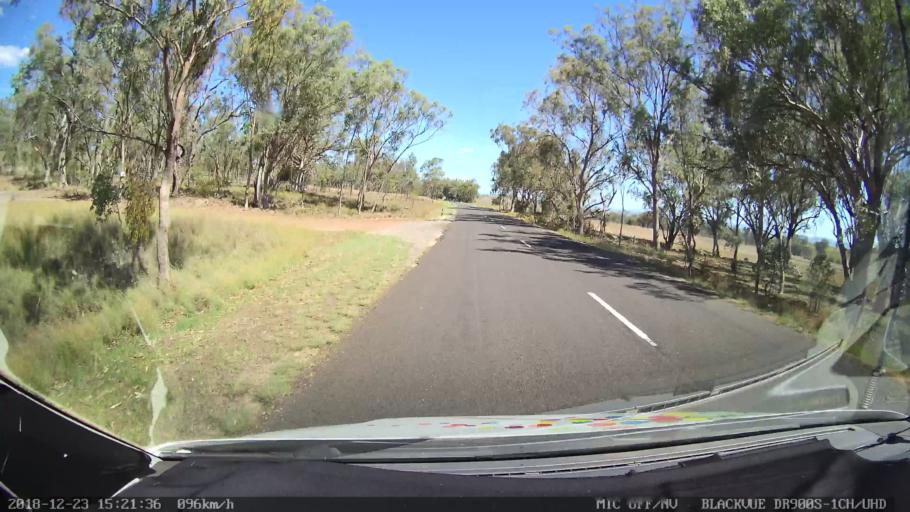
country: AU
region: New South Wales
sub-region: Tamworth Municipality
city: Manilla
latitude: -30.8586
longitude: 150.7977
